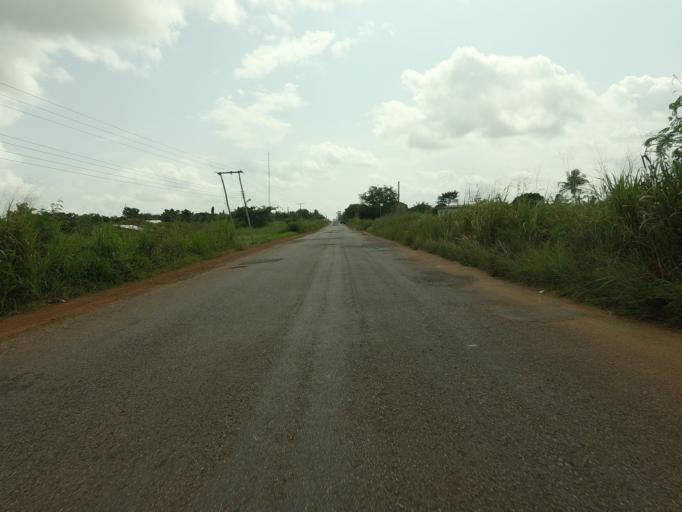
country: TG
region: Maritime
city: Lome
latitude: 6.2247
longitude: 1.0269
